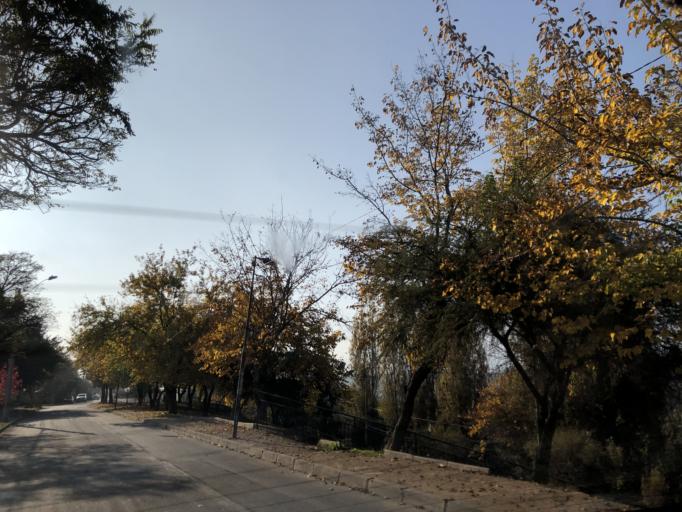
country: CL
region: Santiago Metropolitan
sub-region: Provincia de Cordillera
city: Puente Alto
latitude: -33.6243
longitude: -70.5770
